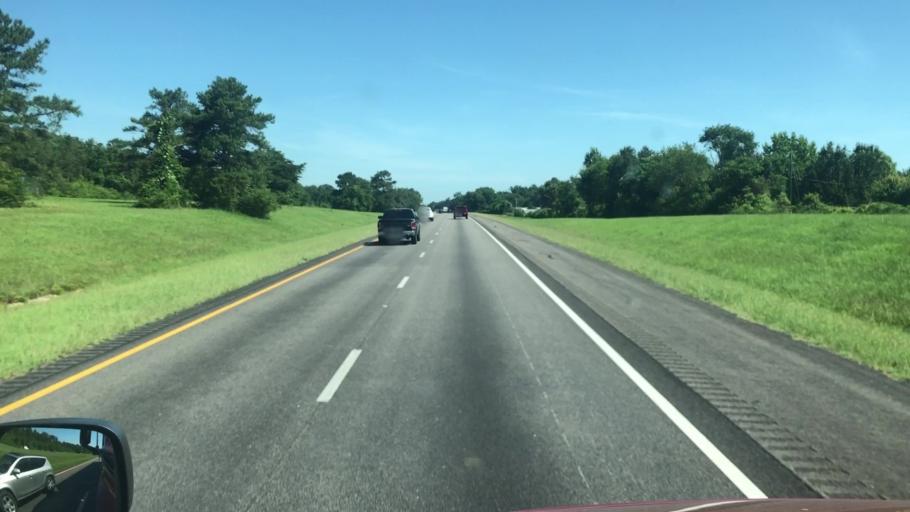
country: US
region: Alabama
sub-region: Autauga County
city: Pine Level
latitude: 32.5638
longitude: -86.4638
